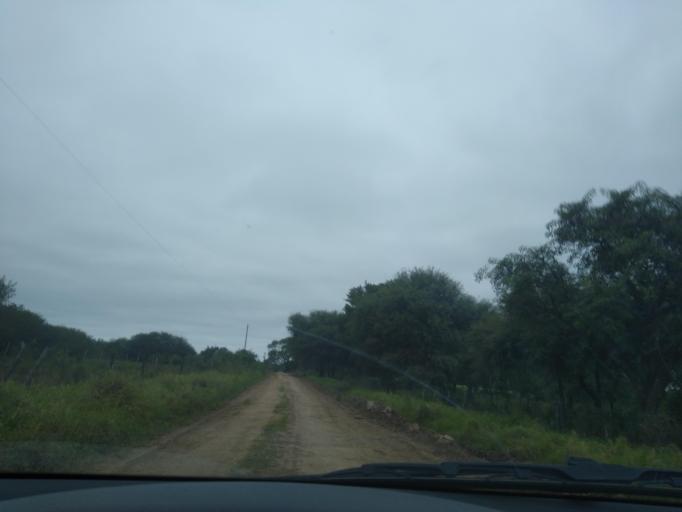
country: AR
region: Chaco
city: Colonia Benitez
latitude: -27.3759
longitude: -58.9422
